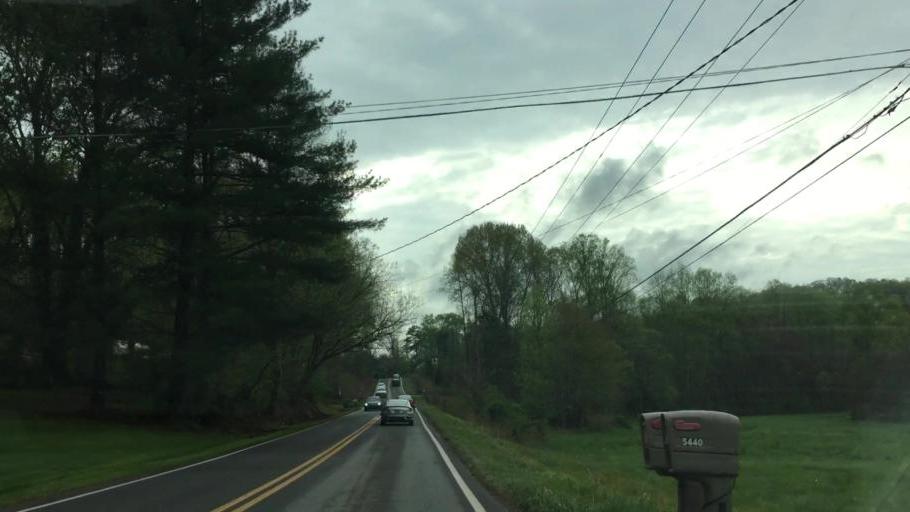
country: US
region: Georgia
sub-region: Fulton County
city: Milton
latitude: 34.1993
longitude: -84.3684
